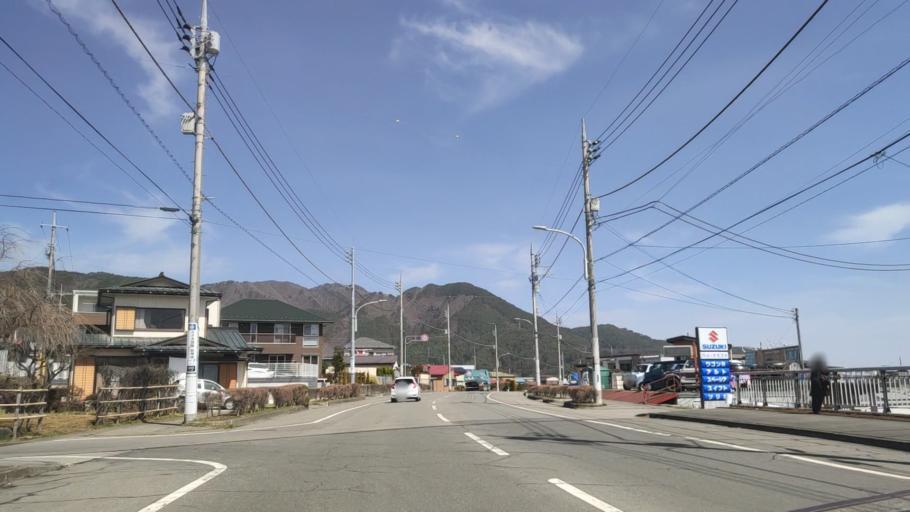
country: JP
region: Yamanashi
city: Fujikawaguchiko
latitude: 35.4876
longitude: 138.7899
